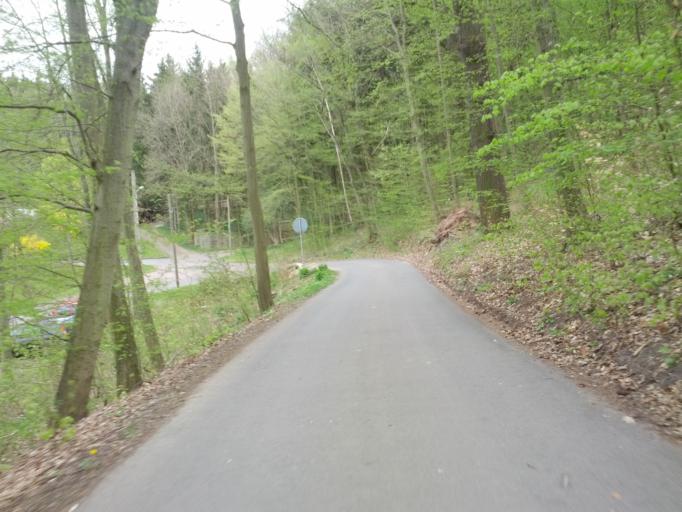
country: DE
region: Thuringia
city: Seebach
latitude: 50.9573
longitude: 10.4061
